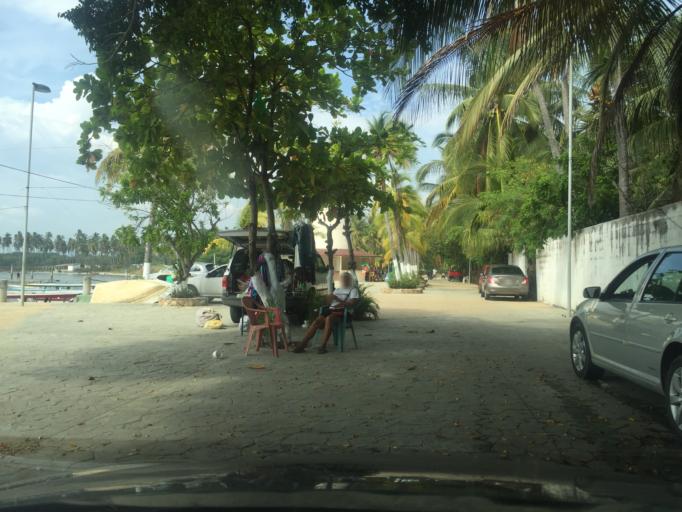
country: MX
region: Guerrero
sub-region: Coyuca de Benitez
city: Colonia Luces en el Mar
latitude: 16.9005
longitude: -99.9680
